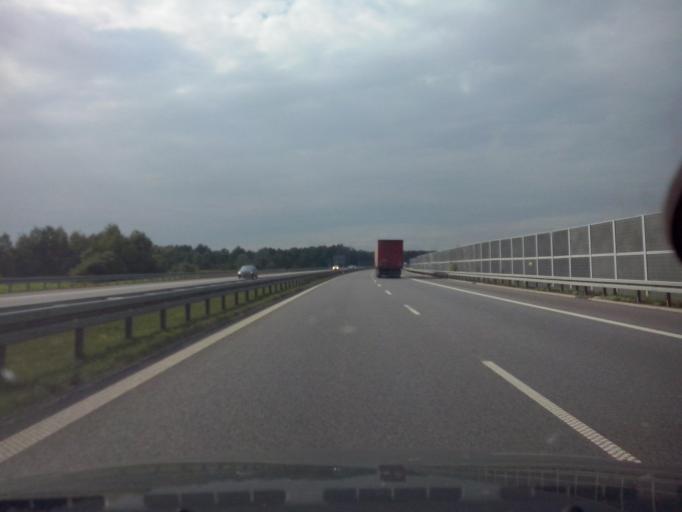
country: PL
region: Lesser Poland Voivodeship
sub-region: Powiat brzeski
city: Jasien
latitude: 49.9927
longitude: 20.5727
